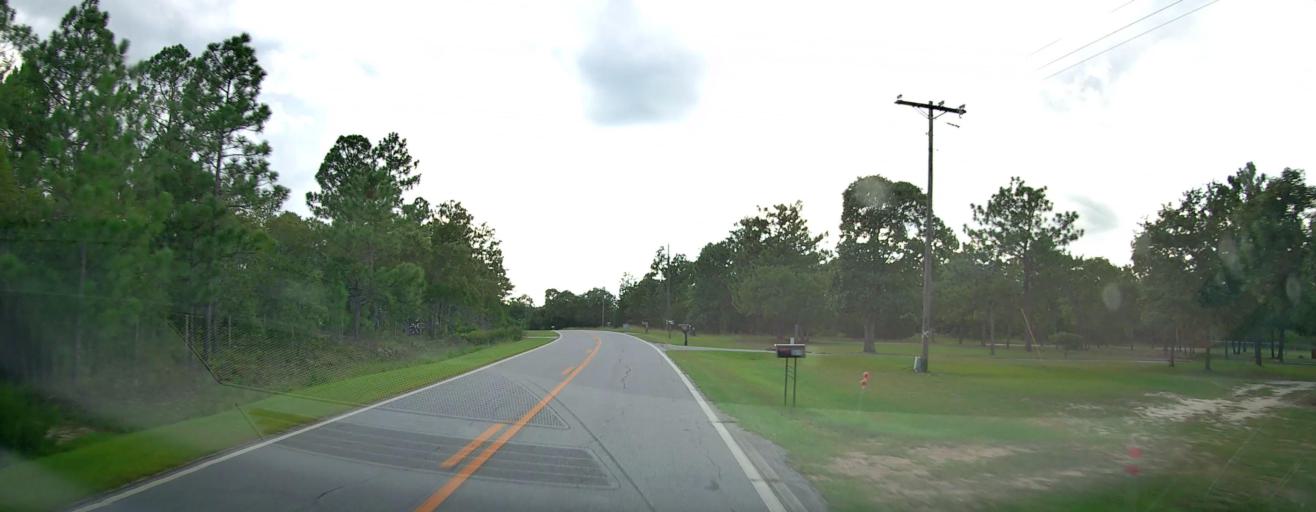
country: US
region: Georgia
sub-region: Bibb County
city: West Point
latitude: 32.7554
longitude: -83.8970
